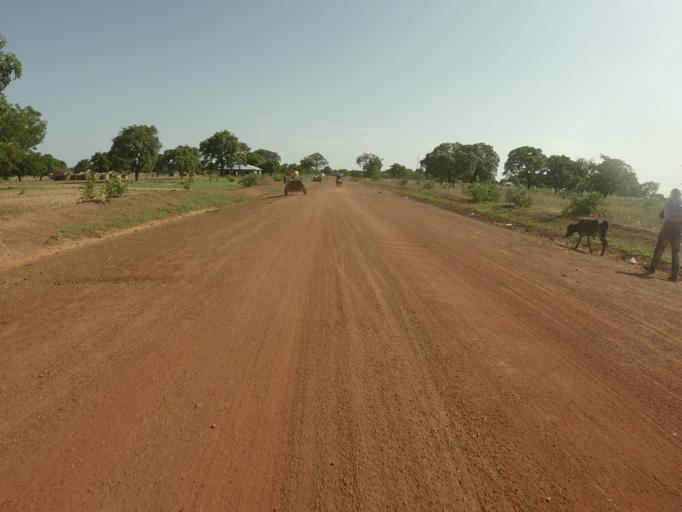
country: GH
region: Upper East
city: Bawku
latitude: 10.7818
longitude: -0.1893
